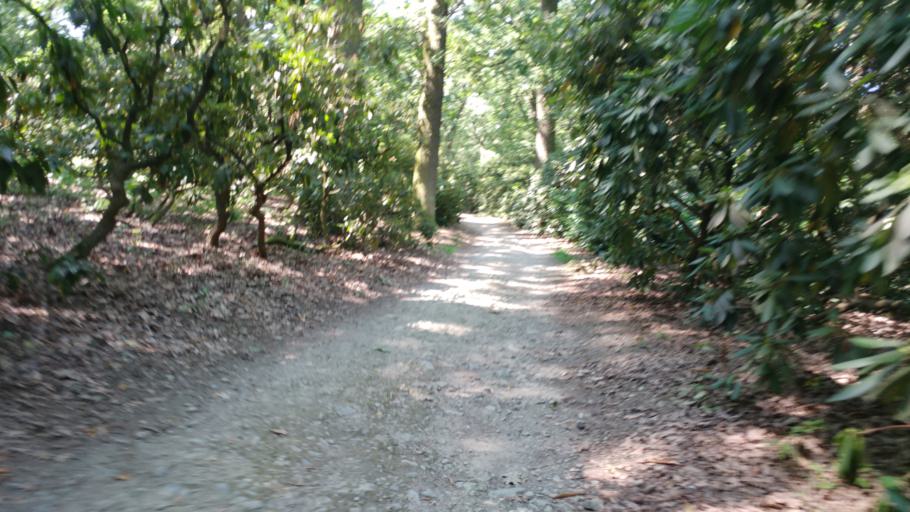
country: CZ
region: Central Bohemia
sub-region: Okres Praha-Zapad
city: Pruhonice
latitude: 49.9955
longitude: 14.5623
